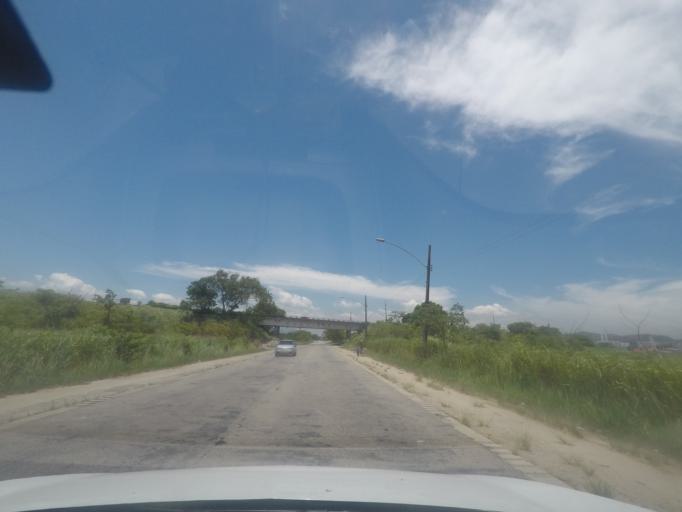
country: BR
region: Rio de Janeiro
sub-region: Itaguai
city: Itaguai
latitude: -22.8961
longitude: -43.6838
